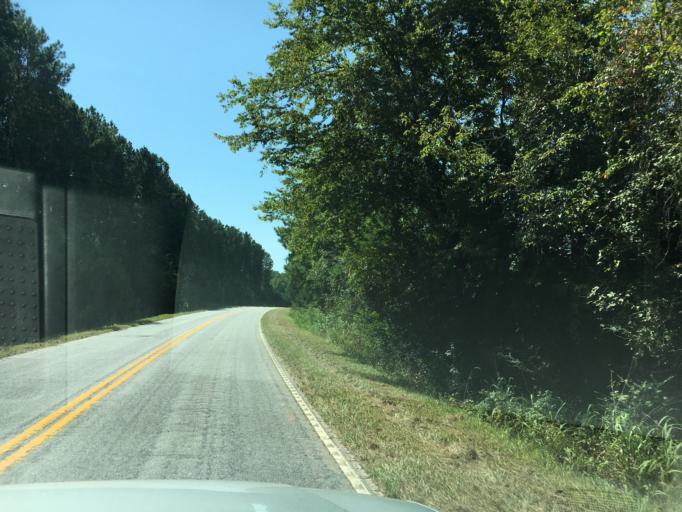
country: US
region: South Carolina
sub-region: Laurens County
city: Clinton
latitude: 34.4343
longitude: -81.8667
